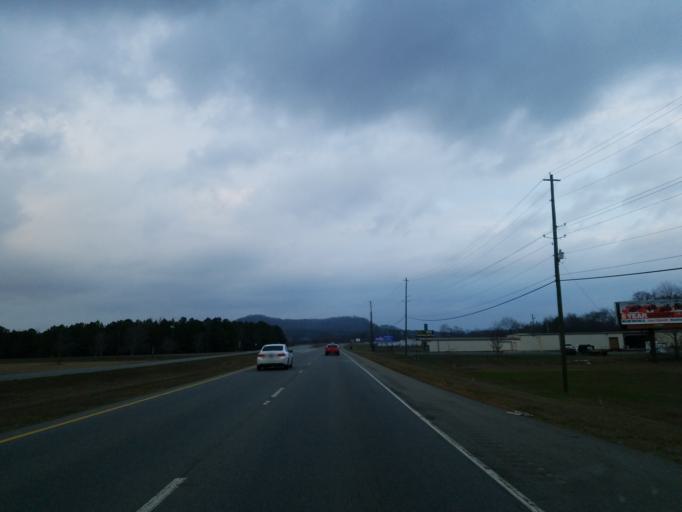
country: US
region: Georgia
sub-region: Bartow County
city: Cartersville
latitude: 34.1356
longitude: -84.8461
